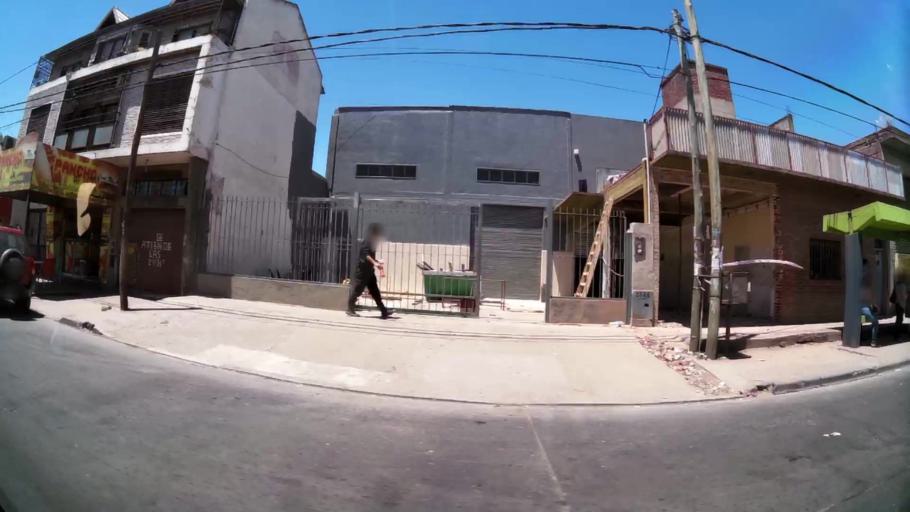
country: AR
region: Buenos Aires
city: Santa Catalina - Dique Lujan
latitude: -34.4963
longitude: -58.7071
